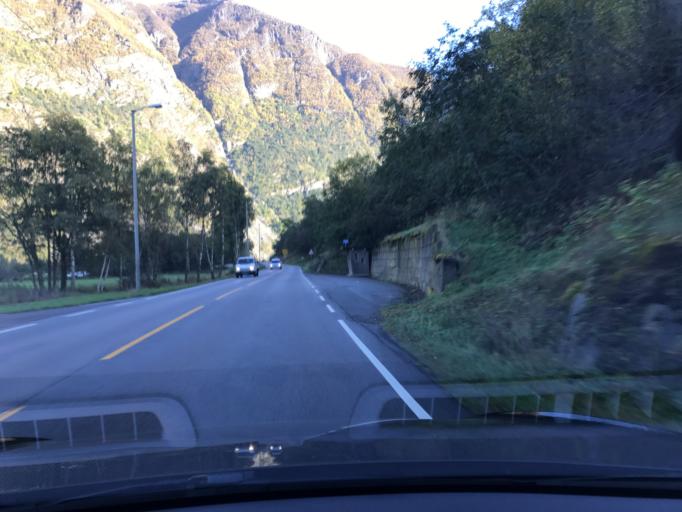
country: NO
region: Sogn og Fjordane
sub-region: Laerdal
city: Laerdalsoyri
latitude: 61.1003
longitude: 7.5087
